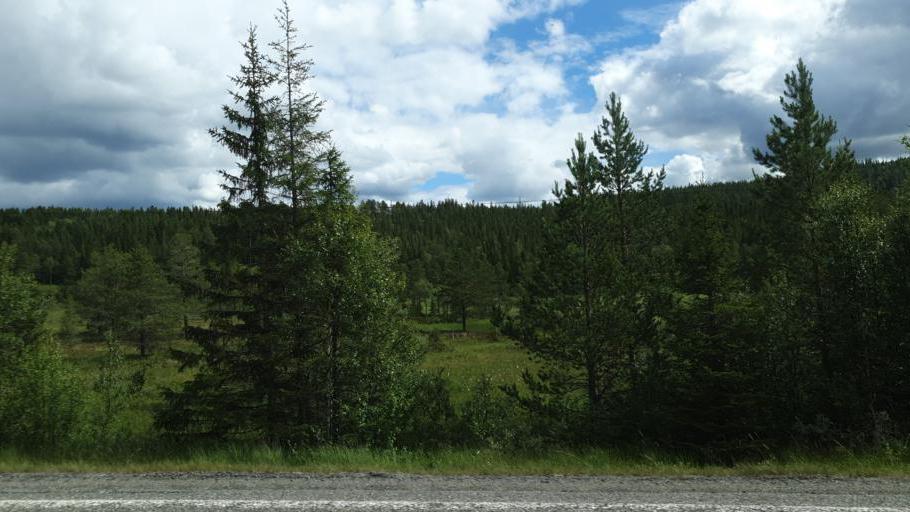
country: NO
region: Sor-Trondelag
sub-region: Rennebu
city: Berkak
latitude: 62.8512
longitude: 10.0197
